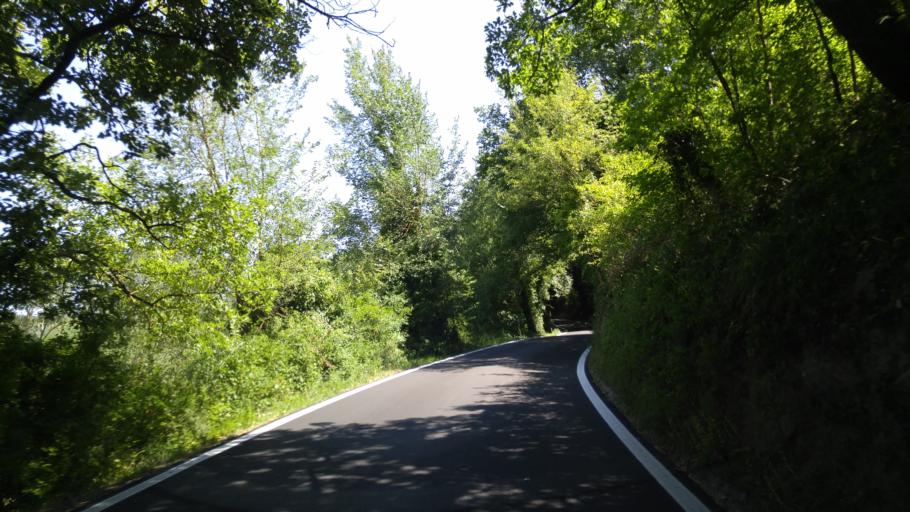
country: IT
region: The Marches
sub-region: Provincia di Pesaro e Urbino
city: Fenile
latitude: 43.8317
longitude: 12.9574
